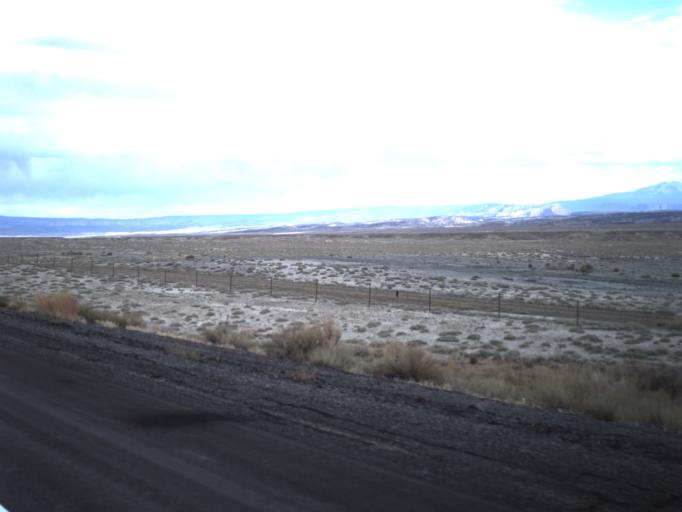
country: US
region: Utah
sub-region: Grand County
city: Moab
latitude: 38.9345
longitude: -109.4604
